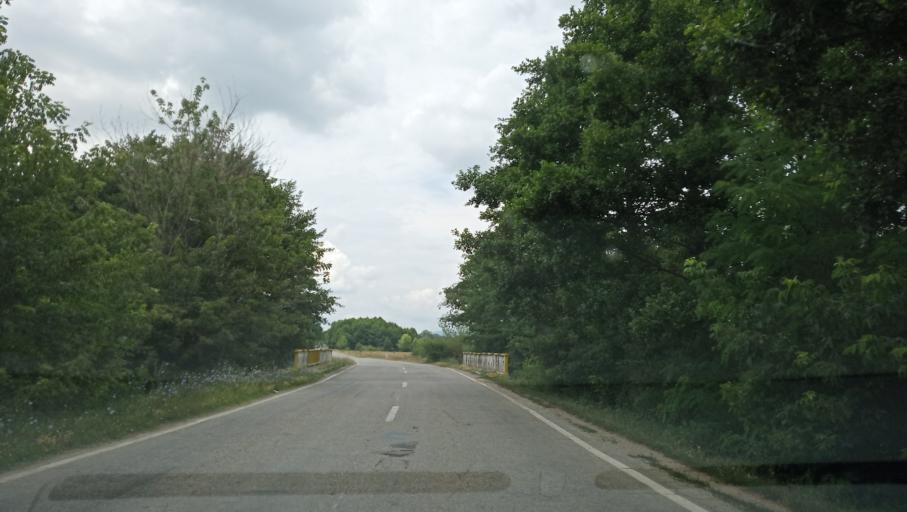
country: RO
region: Gorj
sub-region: Comuna Runcu
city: Valea Mare
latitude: 45.0863
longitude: 23.0771
